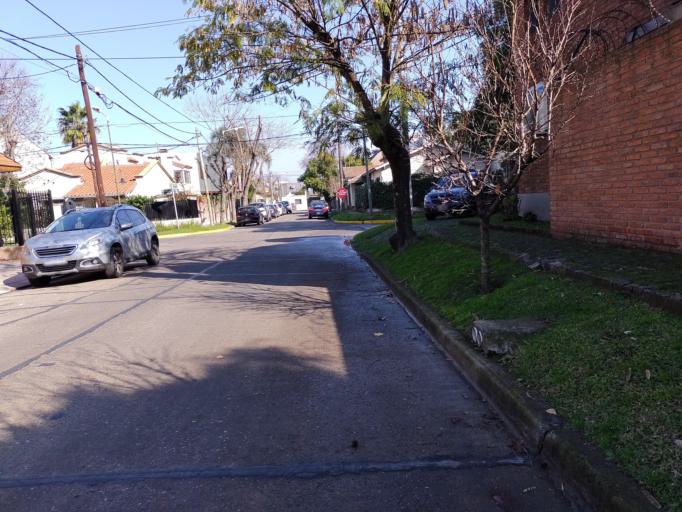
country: AR
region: Buenos Aires
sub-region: Partido de San Isidro
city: San Isidro
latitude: -34.4498
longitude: -58.5350
